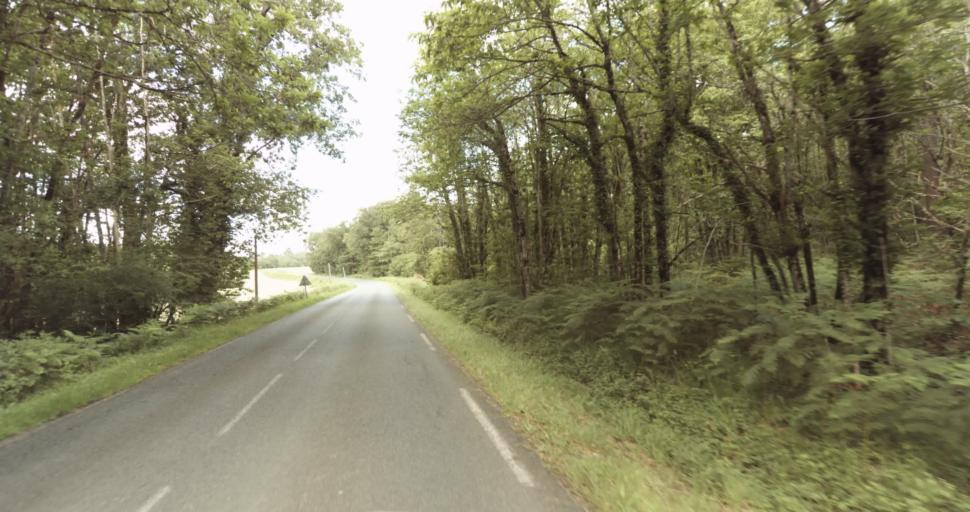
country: FR
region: Aquitaine
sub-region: Departement de la Dordogne
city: Beaumont-du-Perigord
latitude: 44.7867
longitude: 0.8379
